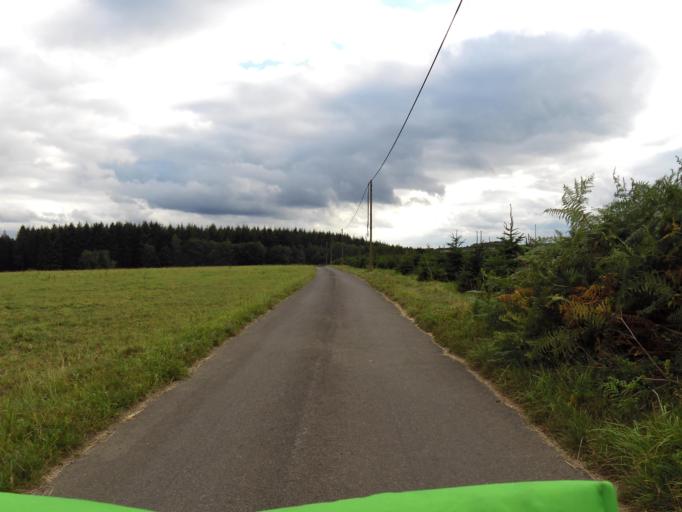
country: BE
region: Wallonia
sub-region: Province de Namur
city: Bievre
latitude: 49.8833
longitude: 4.9985
